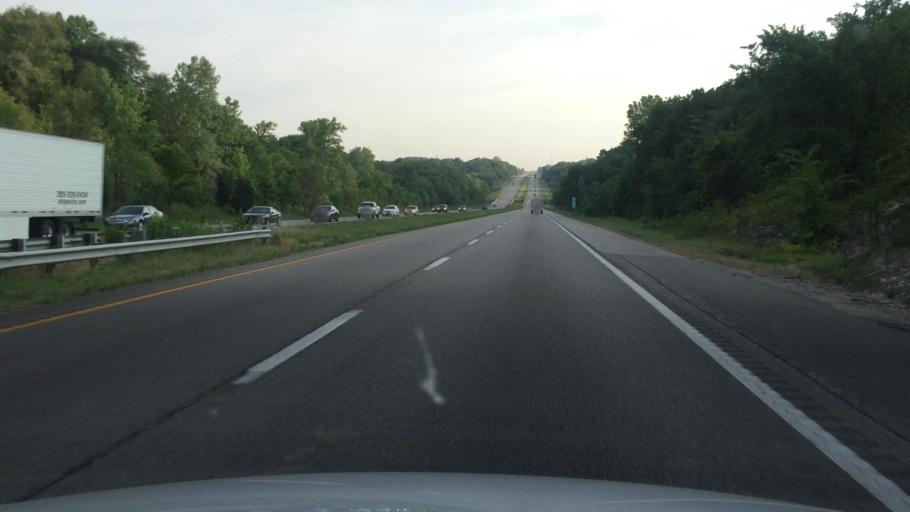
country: US
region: Missouri
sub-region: Buchanan County
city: Saint Joseph
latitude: 39.6520
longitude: -94.7878
